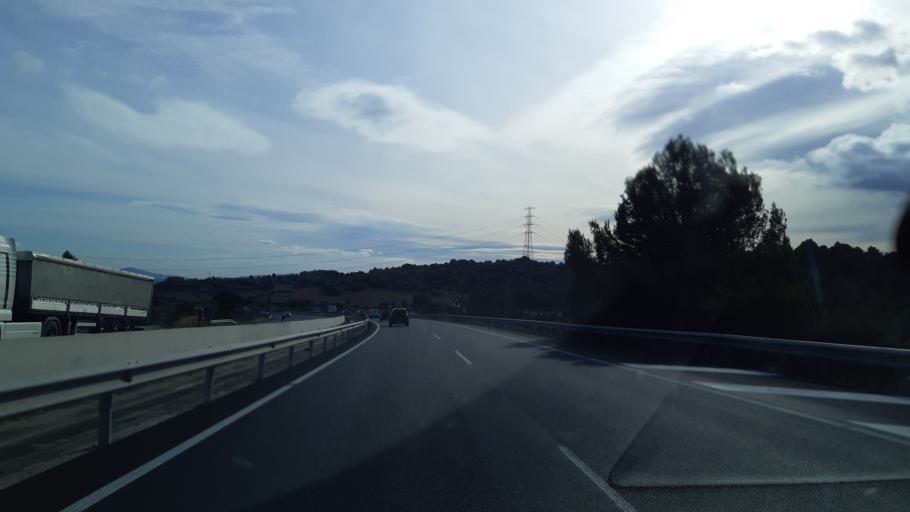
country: ES
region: Catalonia
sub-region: Provincia de Barcelona
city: Collbato
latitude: 41.5577
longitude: 1.8351
